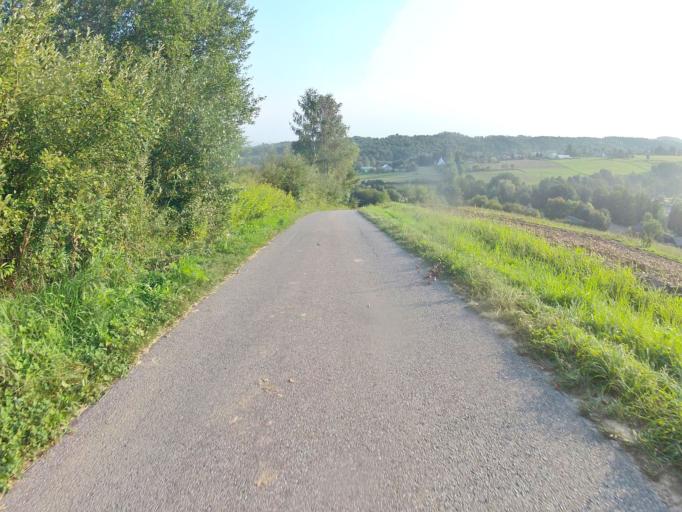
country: PL
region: Subcarpathian Voivodeship
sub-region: Powiat jasielski
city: Brzyska
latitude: 49.7917
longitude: 21.3709
